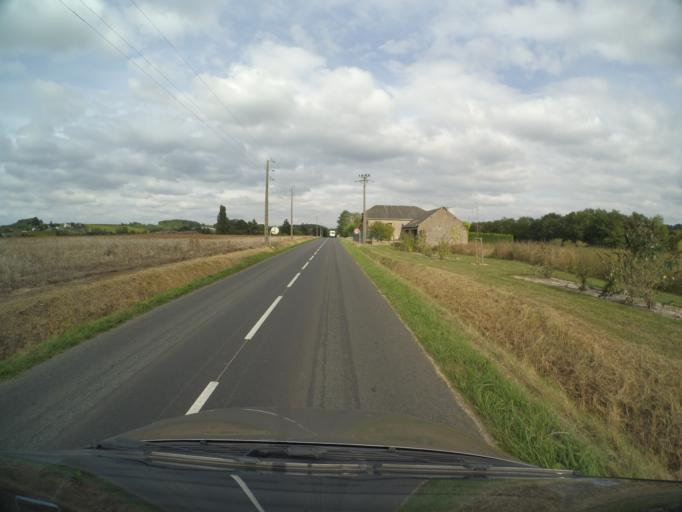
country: FR
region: Centre
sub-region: Departement d'Indre-et-Loire
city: Vernou-sur-Brenne
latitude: 47.4408
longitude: 0.8596
